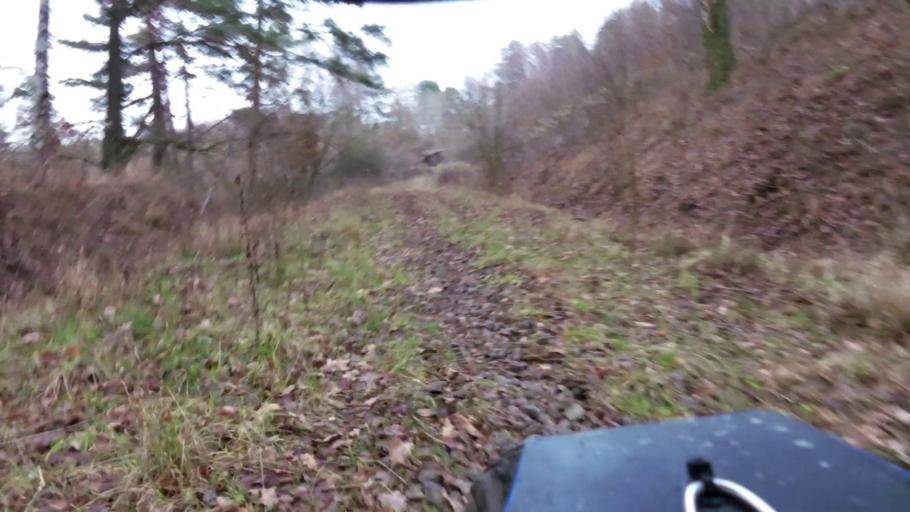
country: PL
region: Lubusz
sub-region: Powiat gorzowski
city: Jenin
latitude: 52.7224
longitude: 15.1264
